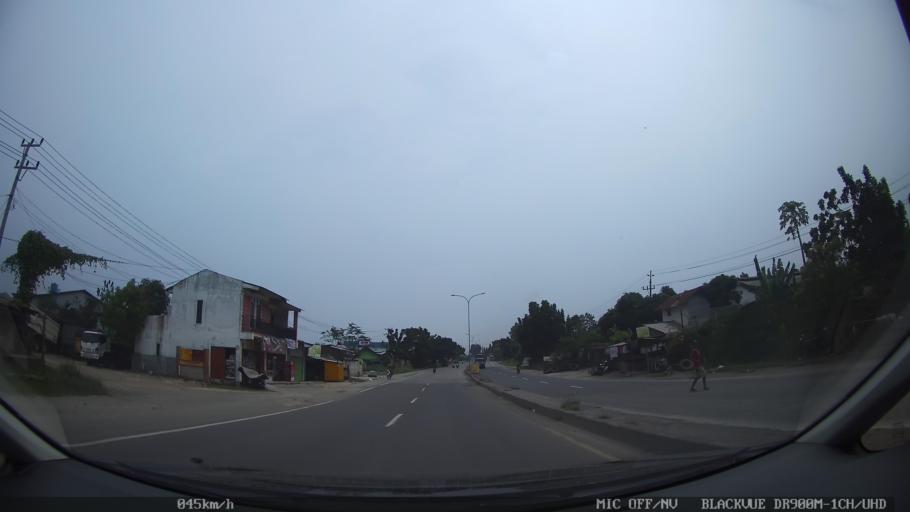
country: ID
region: Lampung
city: Bandarlampung
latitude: -5.4210
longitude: 105.2955
